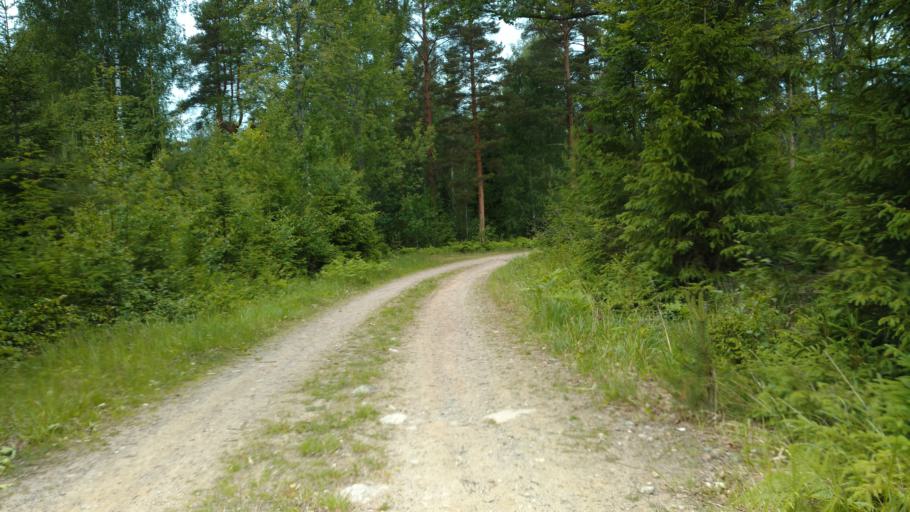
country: FI
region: Uusimaa
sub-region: Raaseporin
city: Pohja
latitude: 60.1166
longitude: 23.5483
